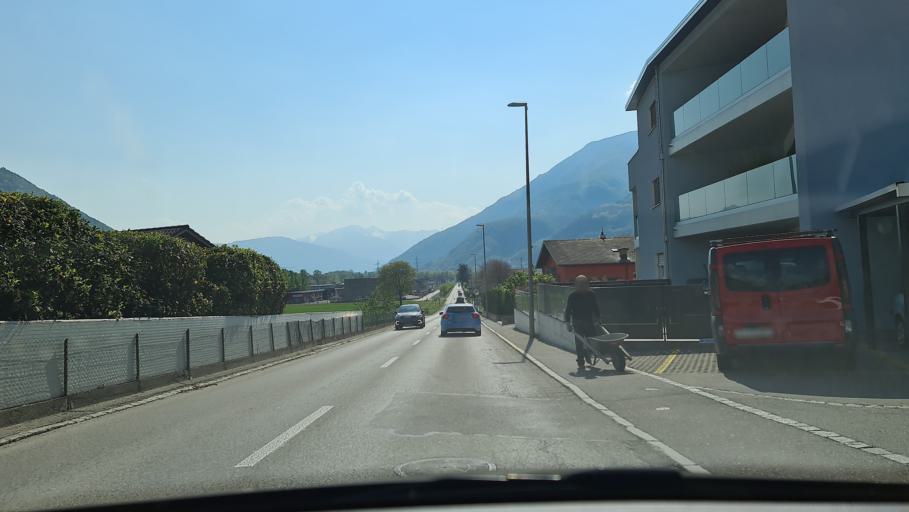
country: CH
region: Ticino
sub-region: Bellinzona District
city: Lumino
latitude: 46.2298
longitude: 9.0623
